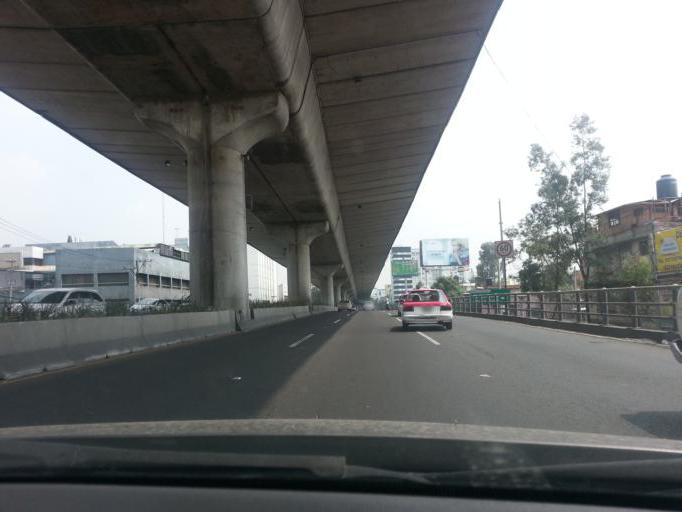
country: MX
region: Mexico City
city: Colonia del Valle
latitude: 19.3888
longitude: -99.1897
